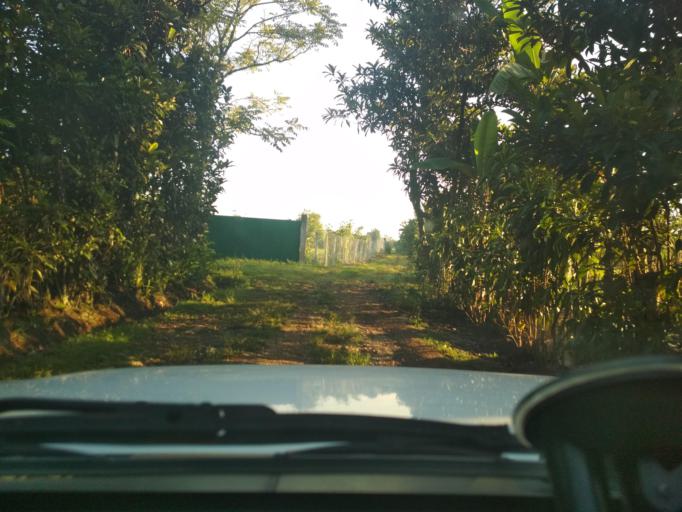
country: MX
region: Veracruz
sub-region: Fortin
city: Fraccionamiento Villas de la Llave
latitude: 18.9226
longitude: -97.0003
